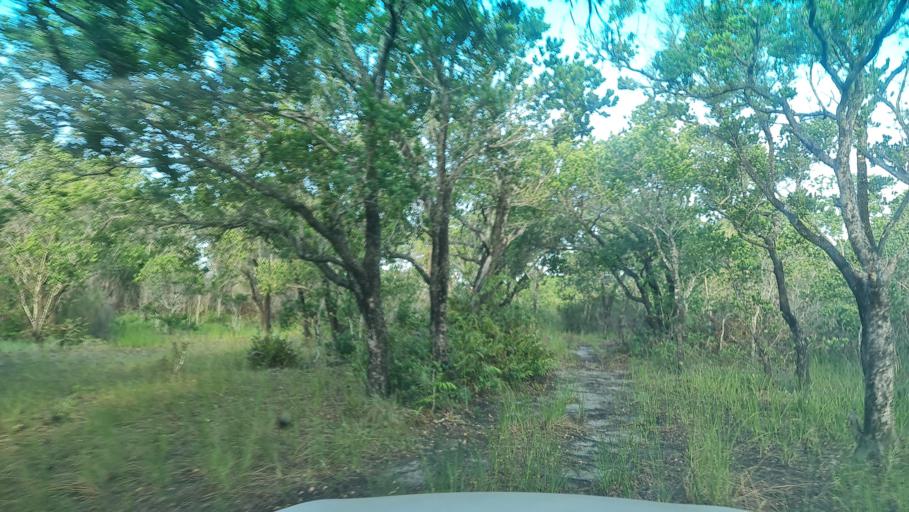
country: MZ
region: Gaza
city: Macia
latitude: -25.2257
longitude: 33.0249
